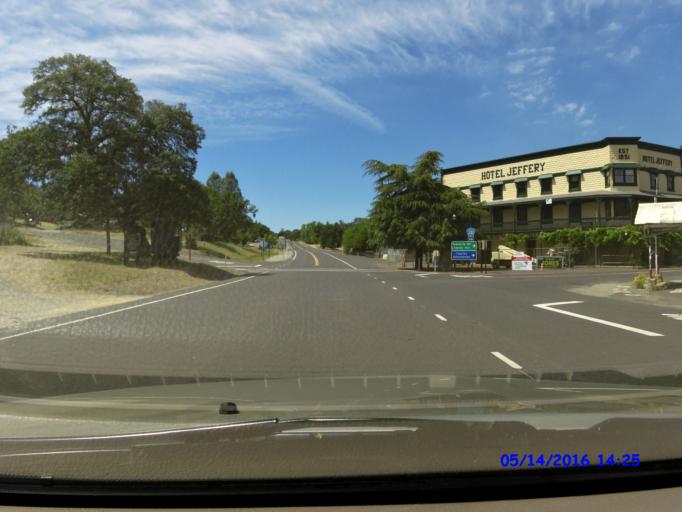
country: US
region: California
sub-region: Tuolumne County
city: Tuolumne City
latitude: 37.7105
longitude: -120.1970
